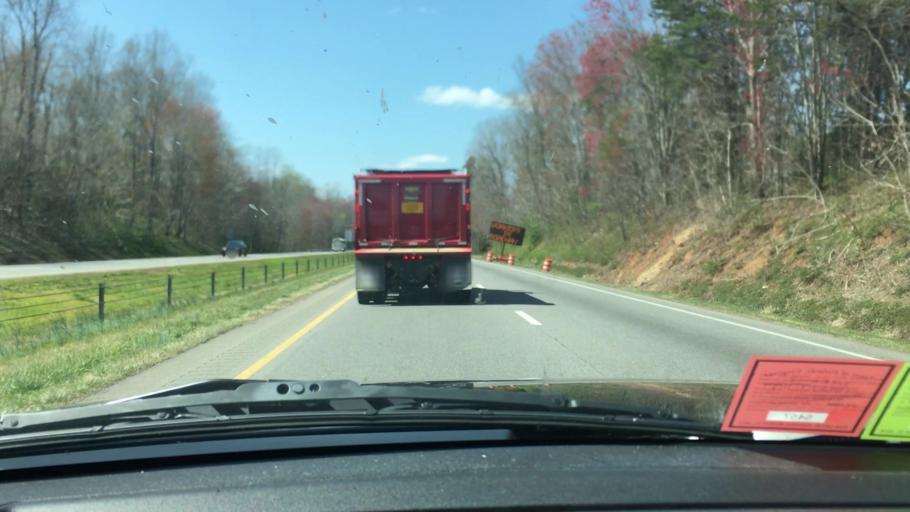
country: US
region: North Carolina
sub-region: Surry County
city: Pilot Mountain
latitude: 36.4331
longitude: -80.5291
